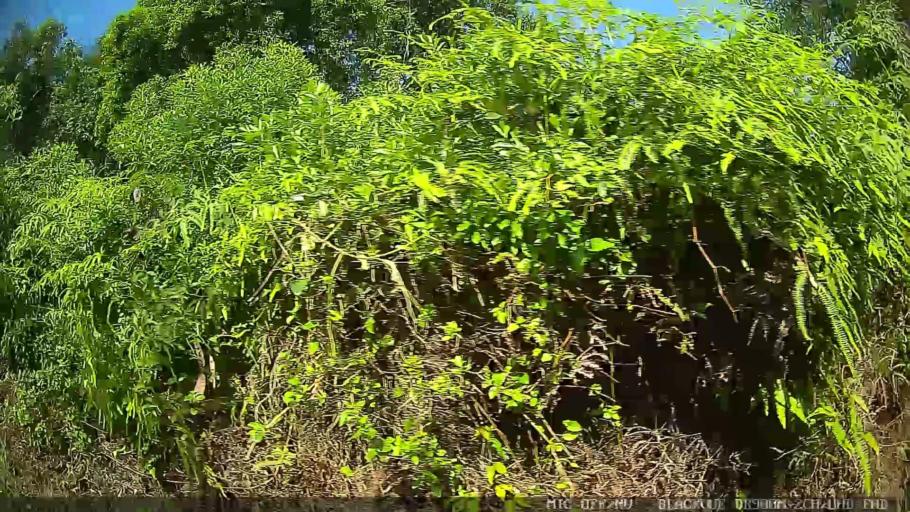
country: BR
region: Sao Paulo
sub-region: Guaruja
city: Guaruja
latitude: -23.9848
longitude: -46.2605
